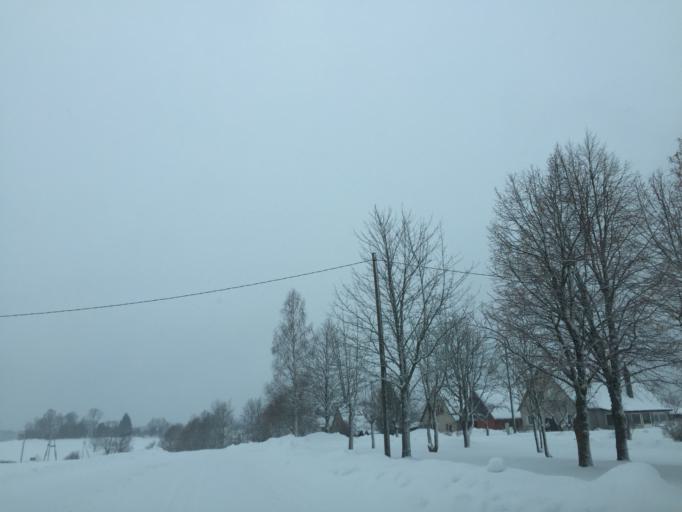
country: LV
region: Amatas Novads
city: Drabesi
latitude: 57.1682
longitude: 25.3213
